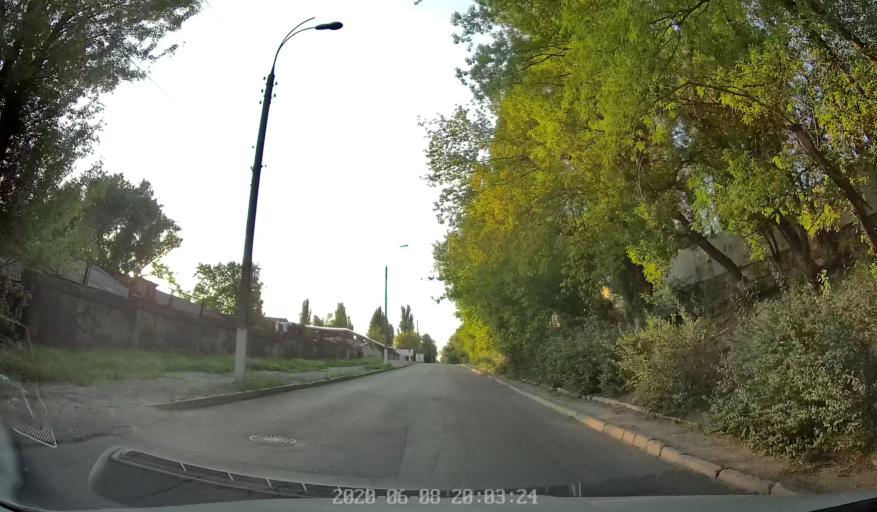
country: MD
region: Chisinau
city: Chisinau
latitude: 47.0142
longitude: 28.8783
